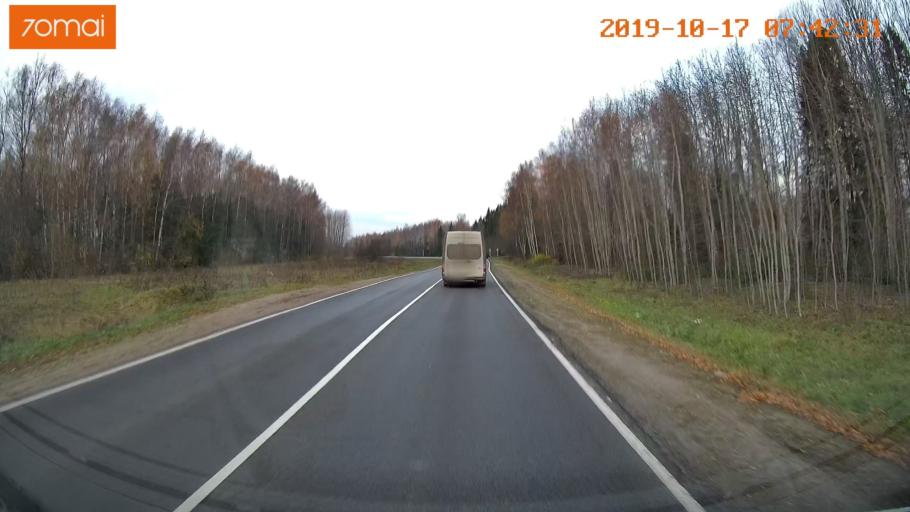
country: RU
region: Vladimir
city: Yur'yev-Pol'skiy
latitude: 56.4844
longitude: 39.7856
